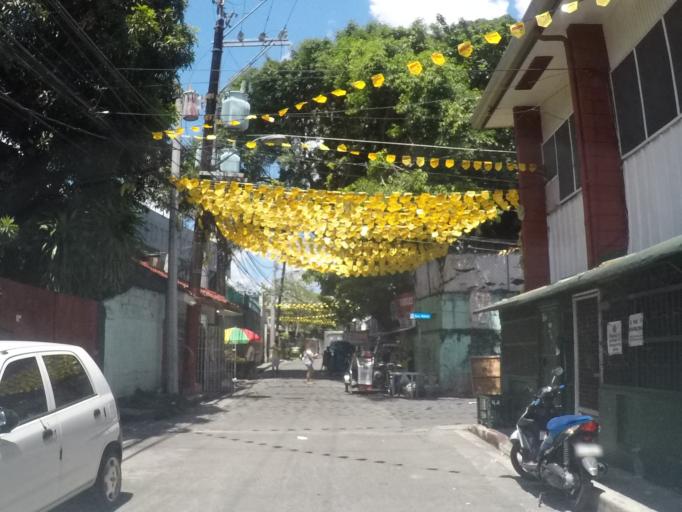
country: PH
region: Metro Manila
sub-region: San Juan
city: San Juan
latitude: 14.6010
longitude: 121.0249
